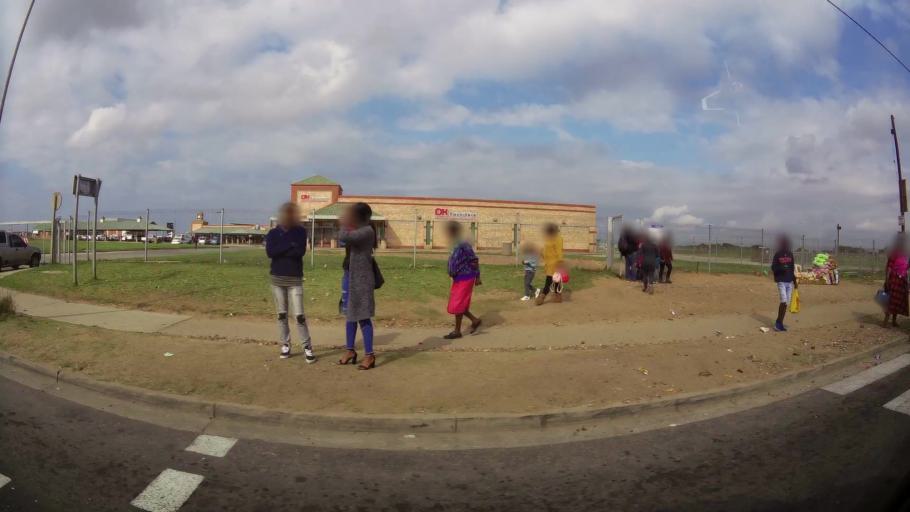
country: ZA
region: Eastern Cape
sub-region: Nelson Mandela Bay Metropolitan Municipality
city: Port Elizabeth
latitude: -33.8102
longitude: 25.5933
